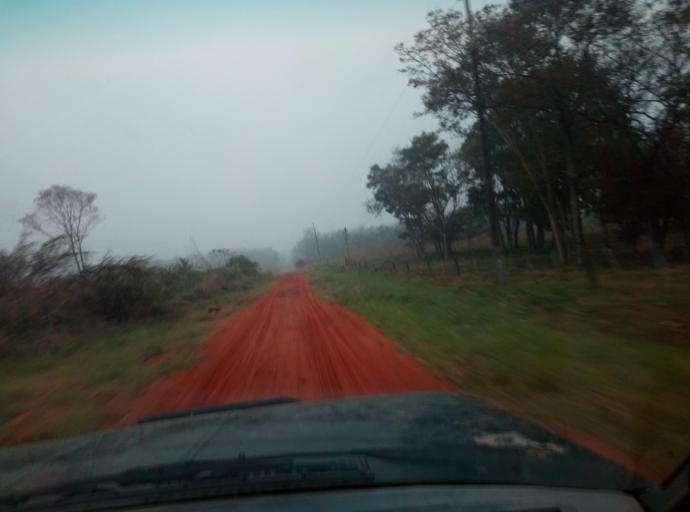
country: PY
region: Caaguazu
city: Doctor Cecilio Baez
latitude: -25.1573
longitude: -56.2738
